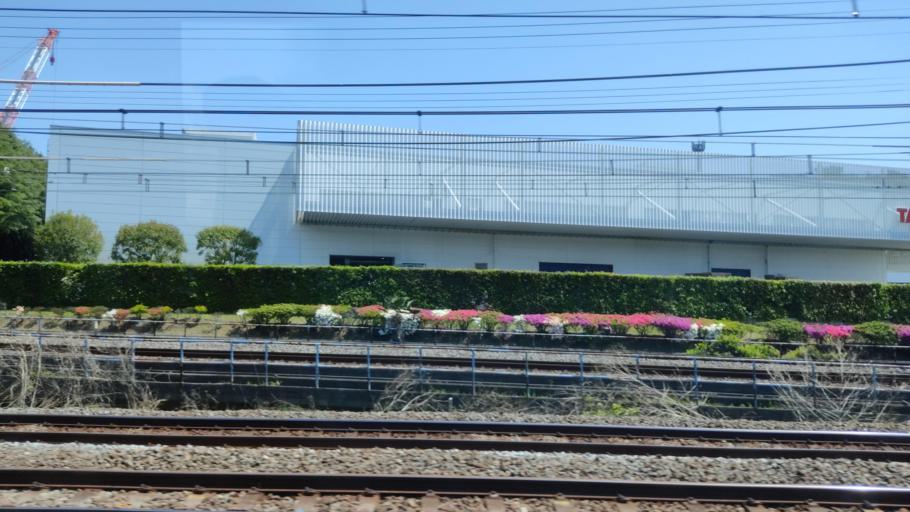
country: JP
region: Kanagawa
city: Kamakura
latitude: 35.3650
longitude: 139.5304
